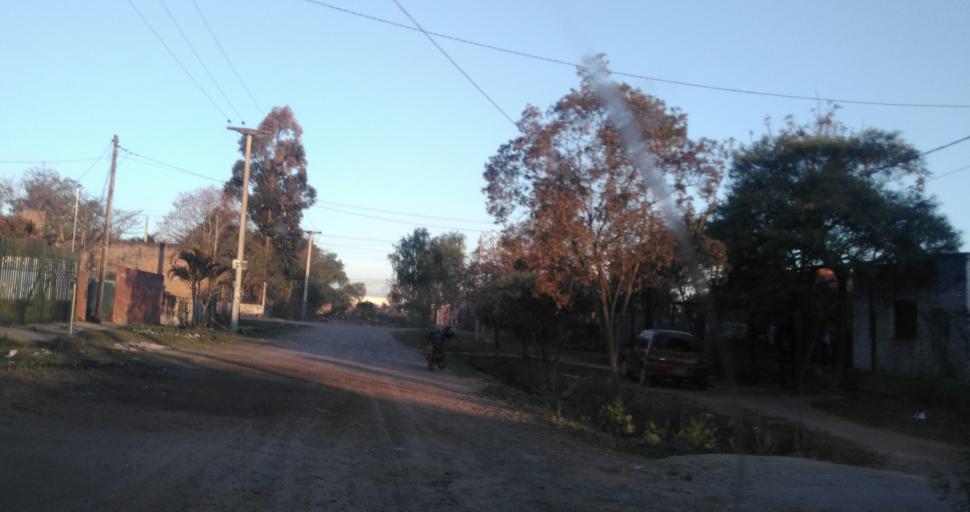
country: AR
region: Chaco
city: Fontana
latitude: -27.4280
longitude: -59.0070
